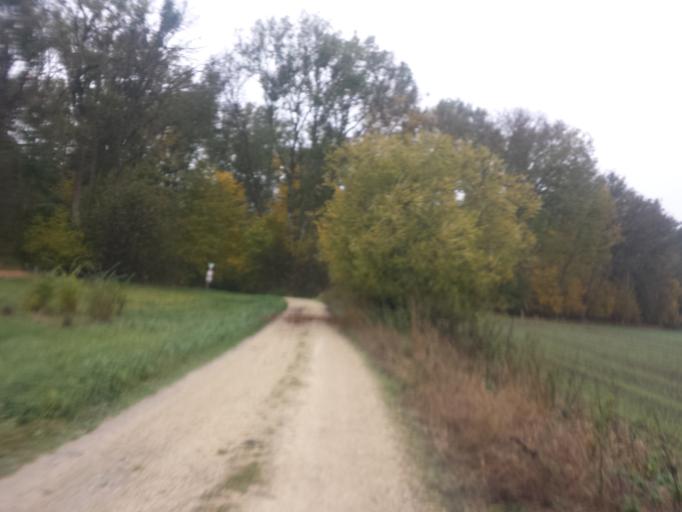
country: DE
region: Bavaria
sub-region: Upper Bavaria
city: Weichering
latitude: 48.7469
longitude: 11.3340
